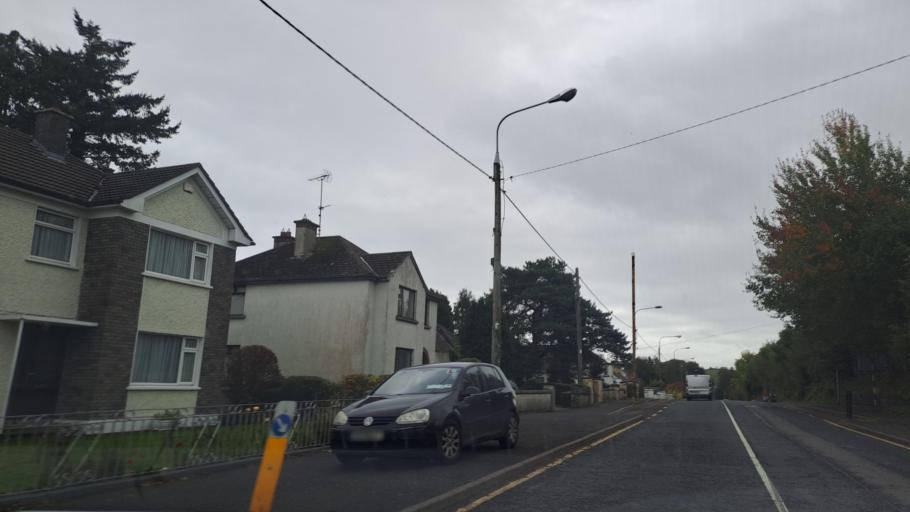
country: IE
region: Ulster
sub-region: An Cabhan
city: Cootehill
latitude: 54.0733
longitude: -7.0747
